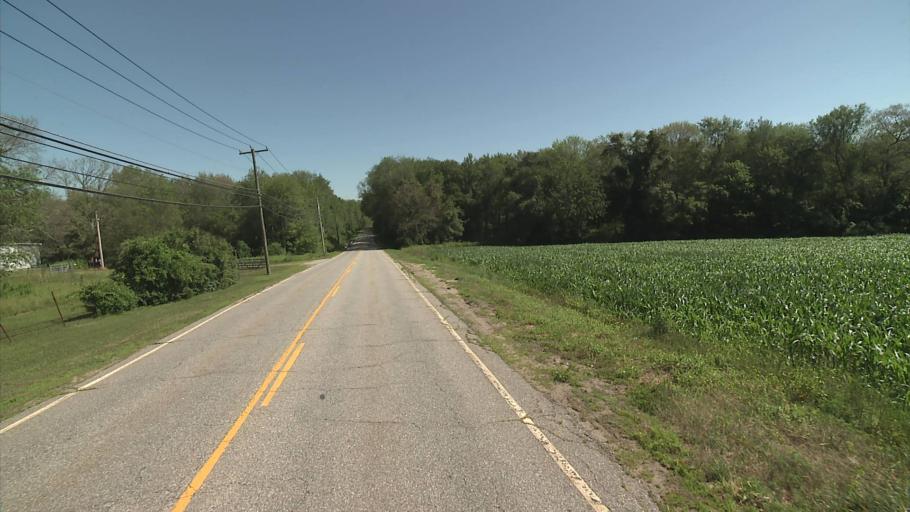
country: US
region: Connecticut
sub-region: New London County
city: Colchester
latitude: 41.6095
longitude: -72.2749
